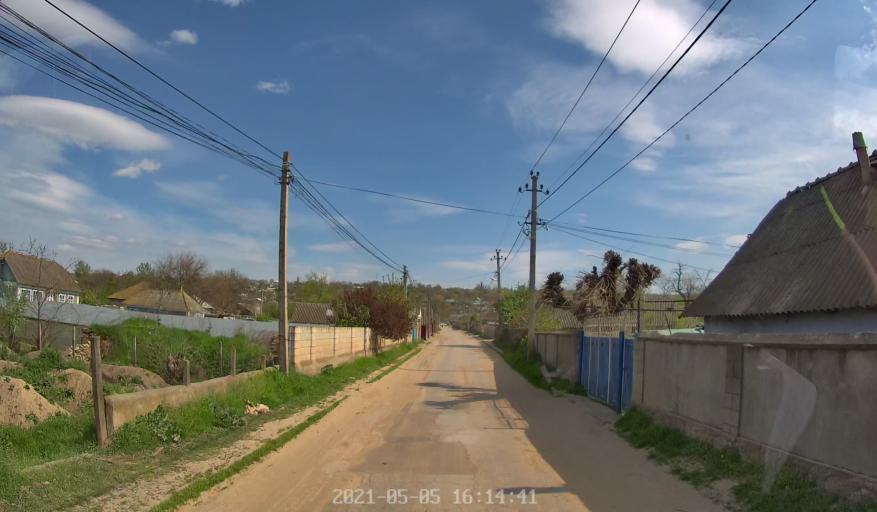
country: MD
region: Criuleni
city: Criuleni
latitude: 47.1363
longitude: 29.2014
